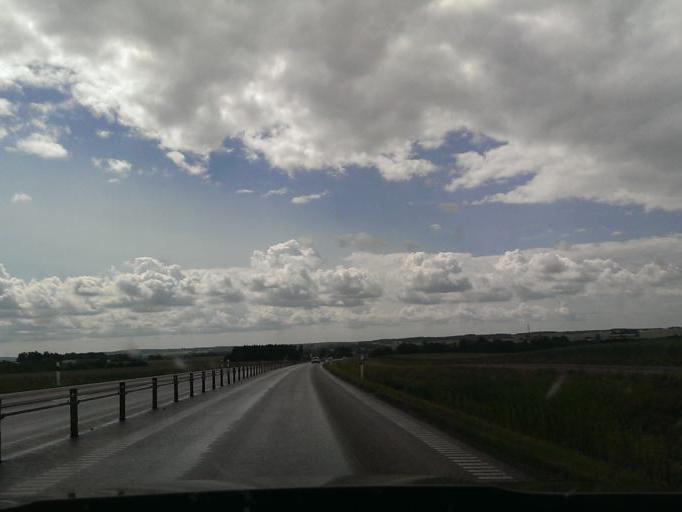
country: SE
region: Skane
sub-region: Eslovs Kommun
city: Eslov
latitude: 55.7813
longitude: 13.3229
